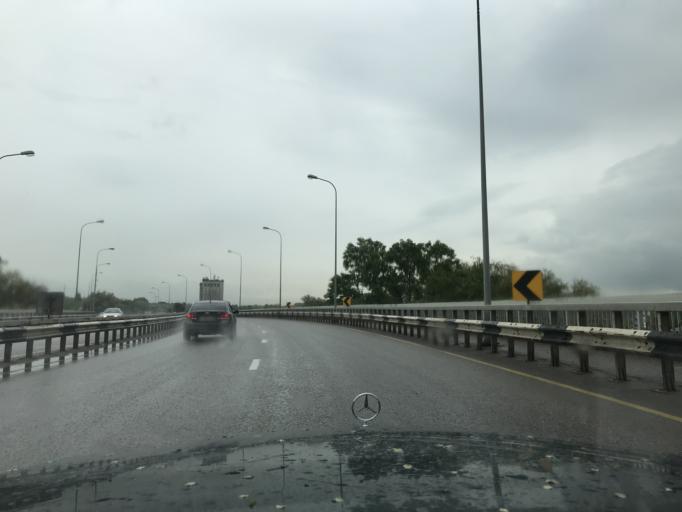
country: KZ
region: Almaty Oblysy
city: Pervomayskiy
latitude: 43.3374
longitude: 76.9638
